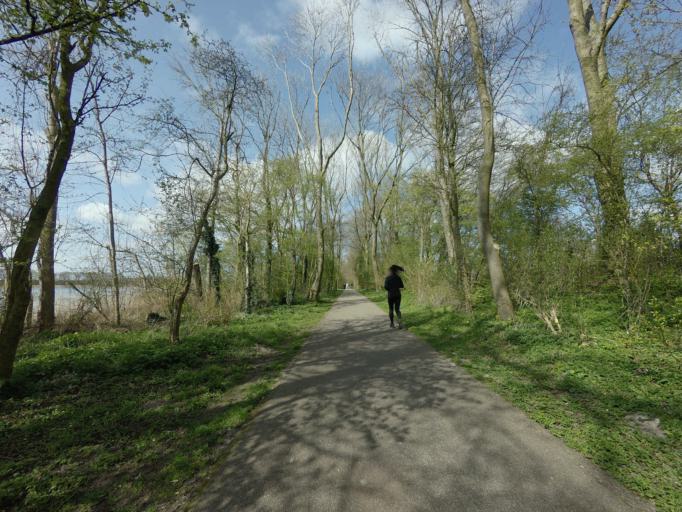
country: NL
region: Utrecht
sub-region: Stichtse Vecht
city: Maarssen
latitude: 52.1408
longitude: 5.0933
